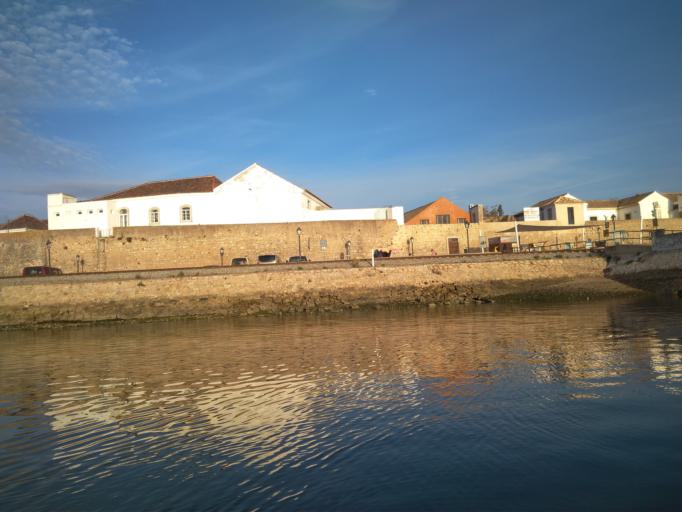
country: PT
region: Faro
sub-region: Faro
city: Faro
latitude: 37.0125
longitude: -7.9363
